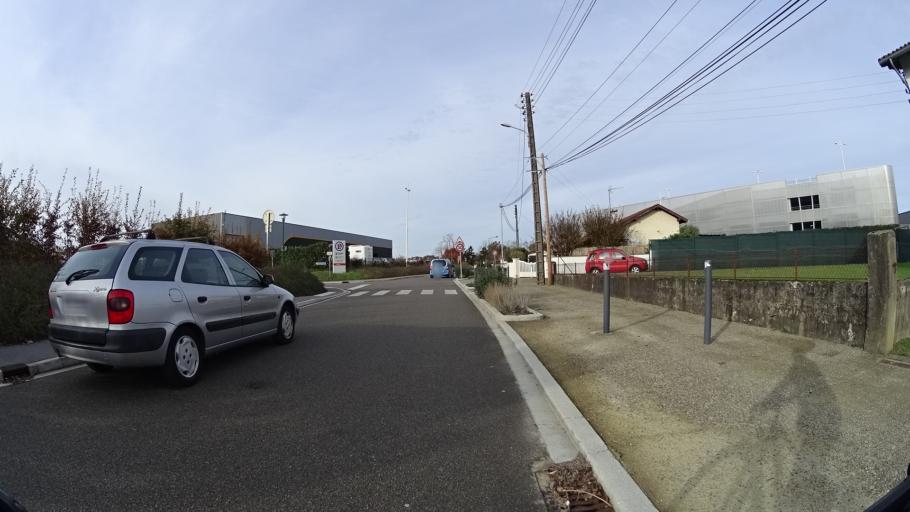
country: FR
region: Aquitaine
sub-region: Departement des Landes
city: Saint-Paul-les-Dax
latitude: 43.7310
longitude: -1.0449
